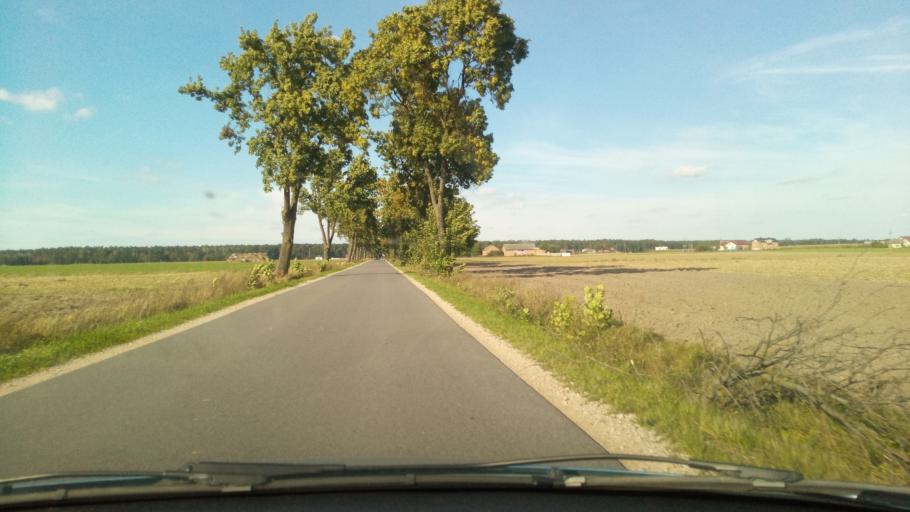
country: PL
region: Lodz Voivodeship
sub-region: Powiat piotrkowski
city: Sulejow
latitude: 51.3978
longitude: 19.8227
